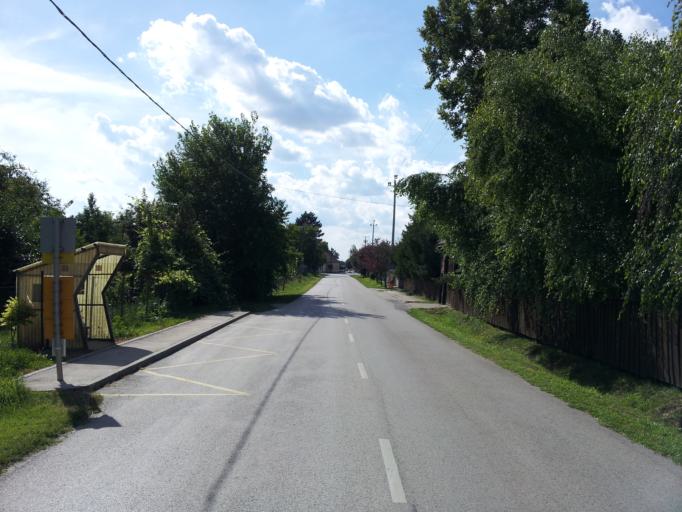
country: HU
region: Pest
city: Szigetcsep
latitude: 47.2625
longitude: 19.0005
